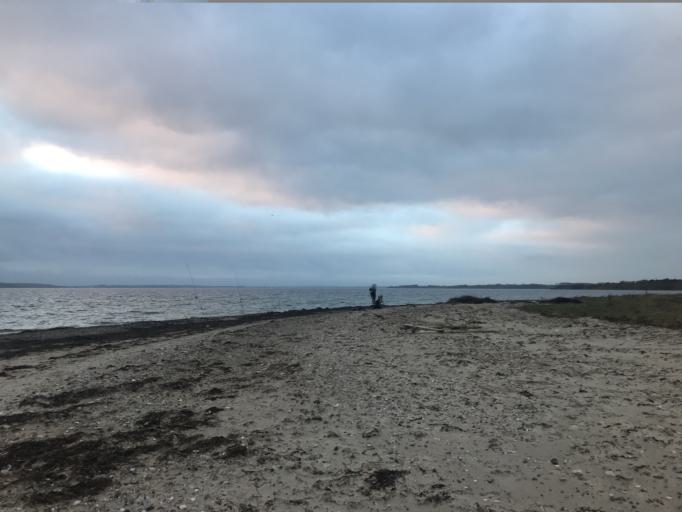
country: DE
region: Schleswig-Holstein
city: Westerholz
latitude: 54.8350
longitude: 9.7271
